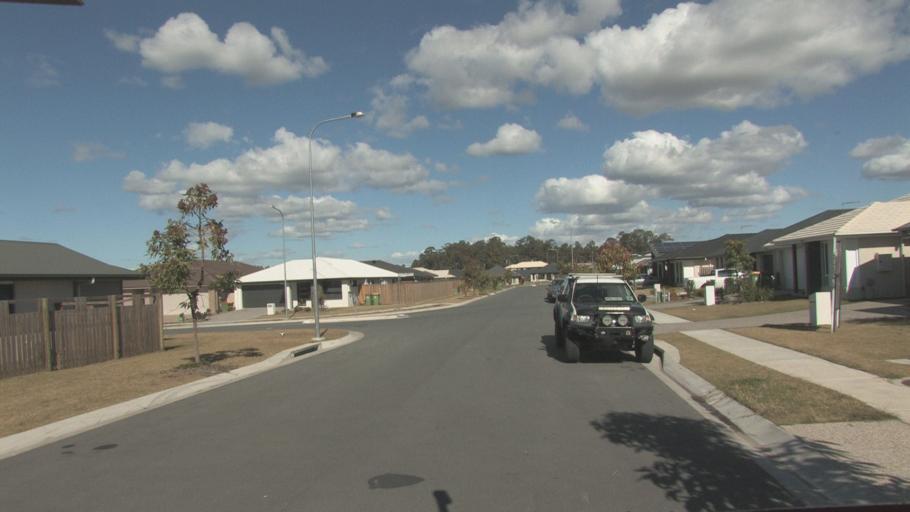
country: AU
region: Queensland
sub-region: Logan
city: Logan Reserve
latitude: -27.7126
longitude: 153.0847
